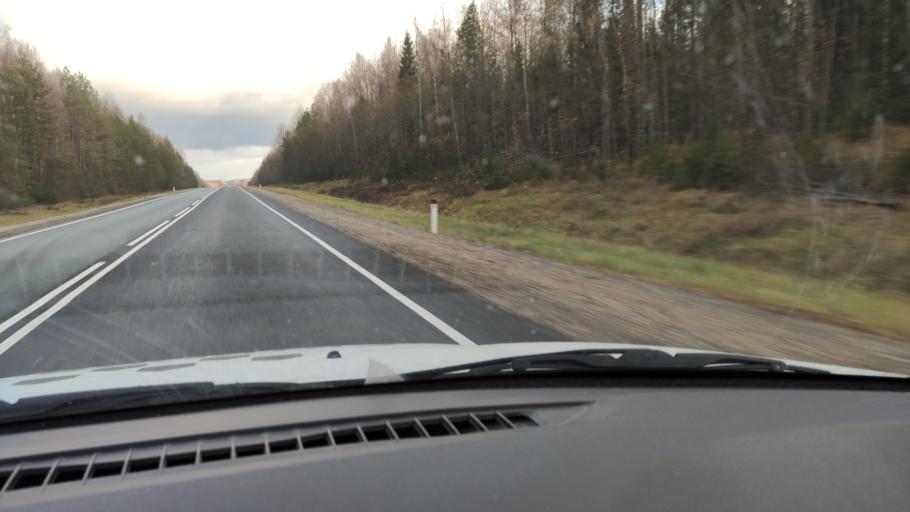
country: RU
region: Kirov
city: Chernaya Kholunitsa
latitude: 58.7985
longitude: 51.8676
